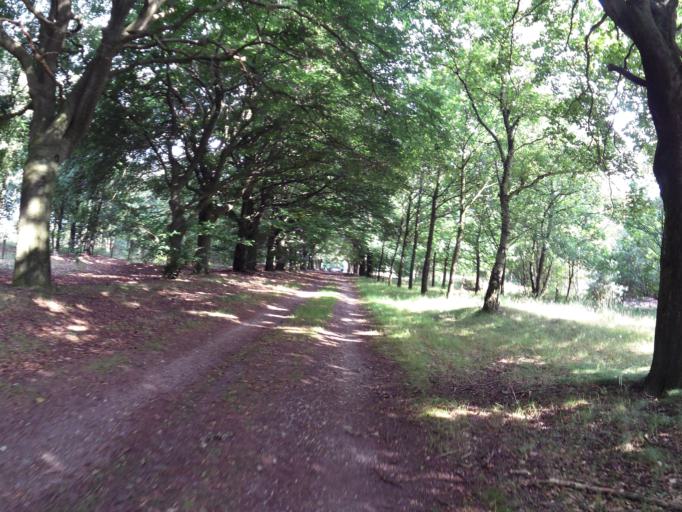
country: NL
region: Gelderland
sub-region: Gemeente Rozendaal
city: Rozendaal
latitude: 52.0465
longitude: 5.9256
